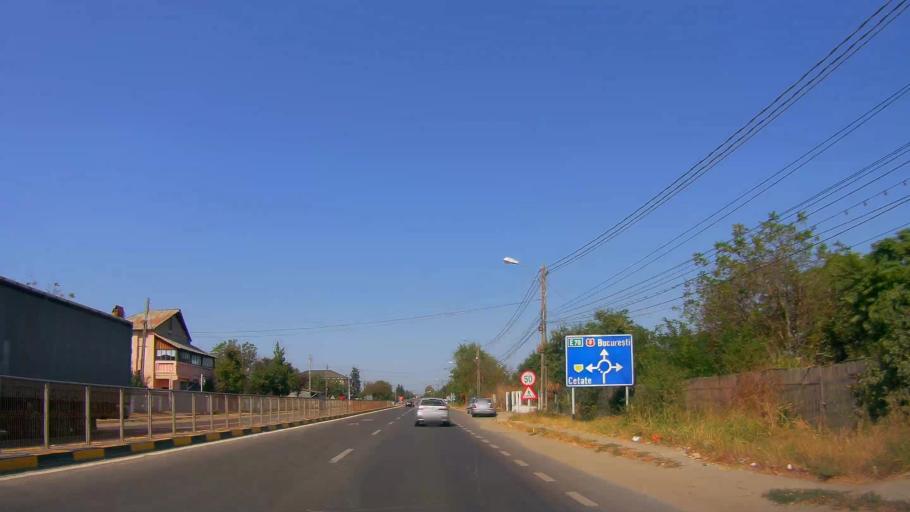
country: RO
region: Giurgiu
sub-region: Comuna Fratesti
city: Remus
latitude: 43.9363
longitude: 25.9773
